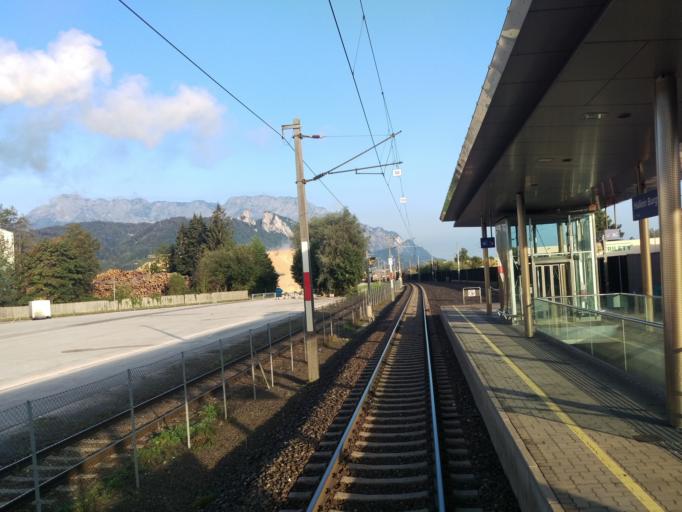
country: AT
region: Salzburg
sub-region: Politischer Bezirk Hallein
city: Hallein
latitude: 47.6760
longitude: 13.1141
